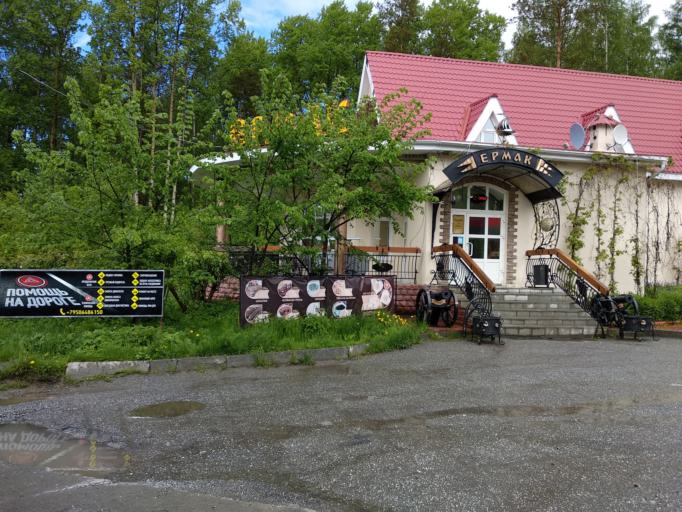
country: RU
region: Sverdlovsk
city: Yelkino
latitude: 58.6395
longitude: 59.9954
